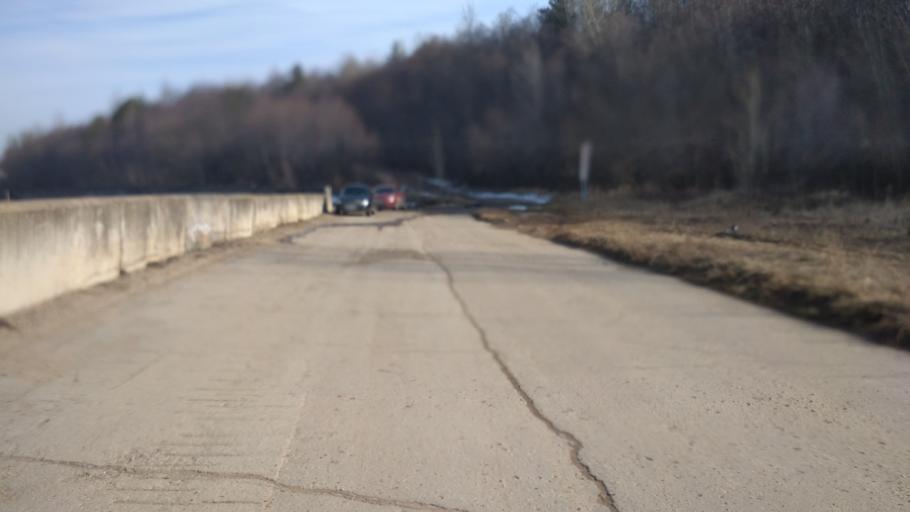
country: RU
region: Chuvashia
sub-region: Cheboksarskiy Rayon
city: Cheboksary
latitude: 56.1446
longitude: 47.3245
